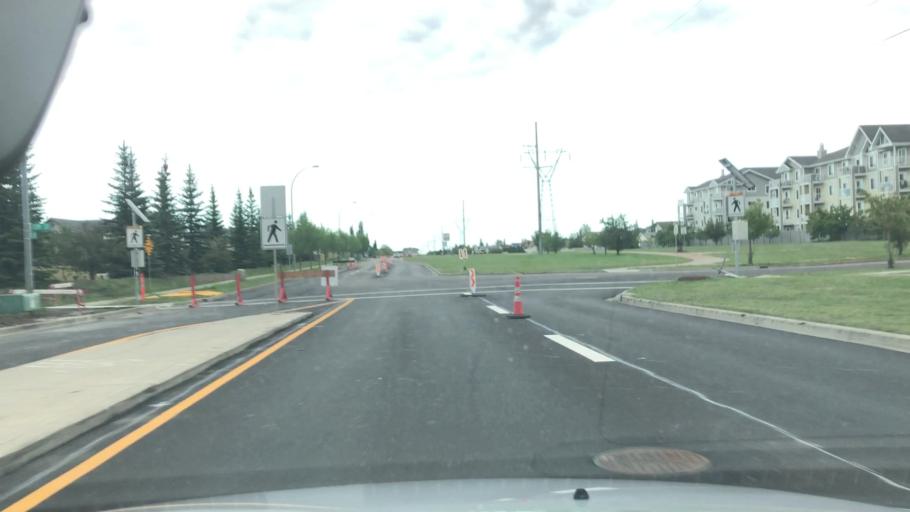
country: CA
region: Alberta
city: St. Albert
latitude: 53.6146
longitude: -113.5606
